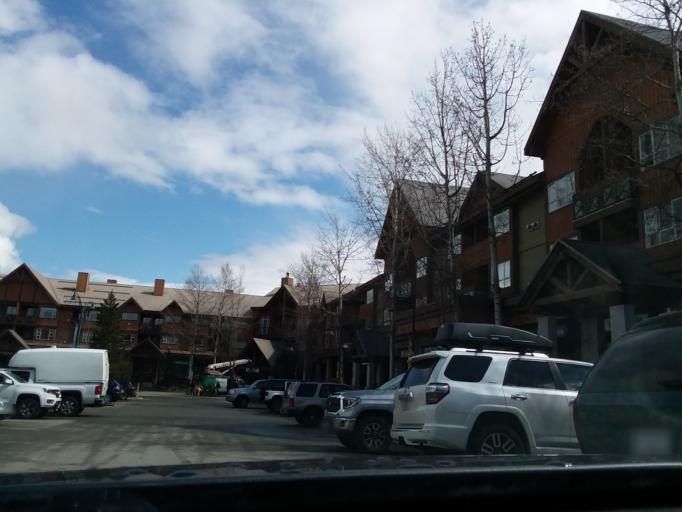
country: CA
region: British Columbia
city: Whistler
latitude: 50.1192
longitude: -122.9568
